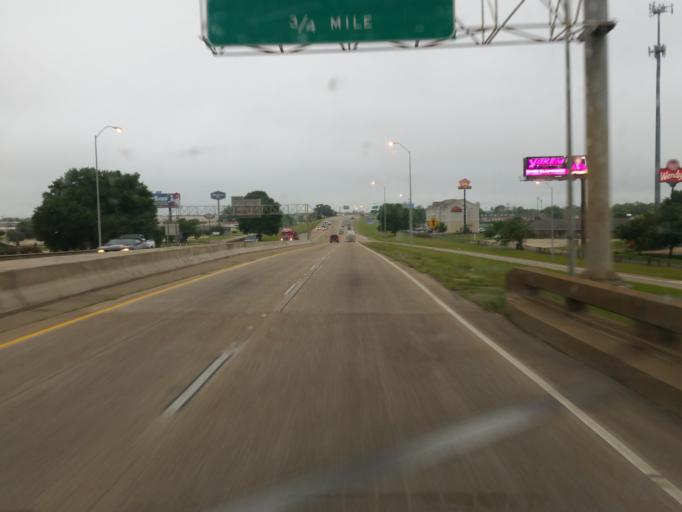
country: US
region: Louisiana
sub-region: Bossier Parish
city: Bossier City
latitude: 32.5181
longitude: -93.7090
